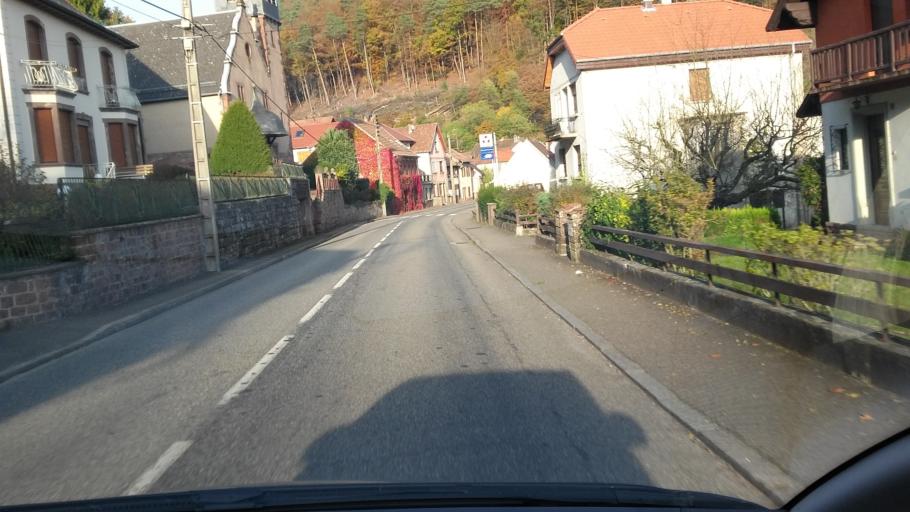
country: FR
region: Lorraine
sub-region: Departement de la Moselle
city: Phalsbourg
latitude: 48.7360
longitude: 7.2508
